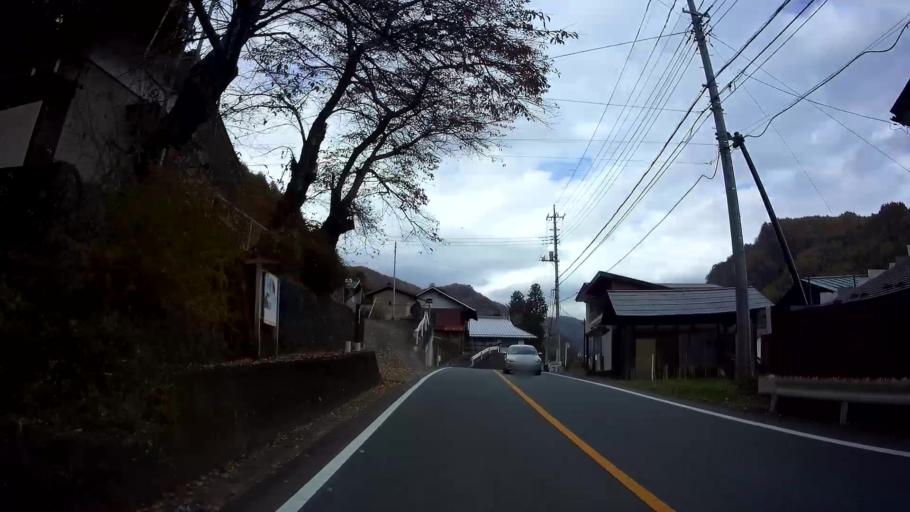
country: JP
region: Gunma
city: Nakanojomachi
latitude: 36.5778
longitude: 138.6231
